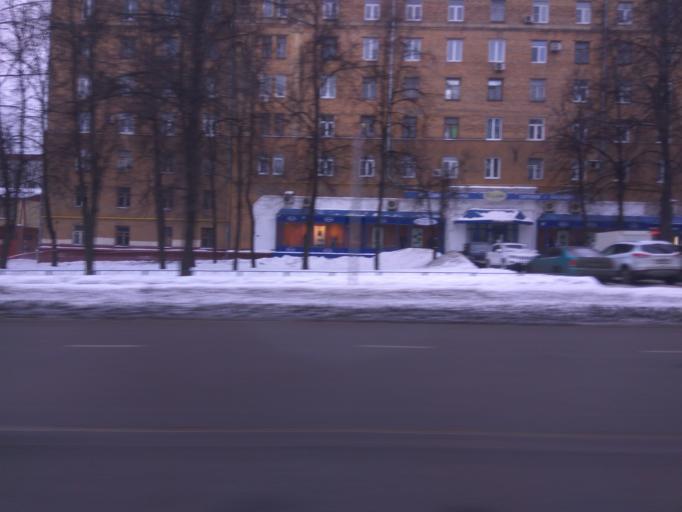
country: RU
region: Moskovskaya
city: Izmaylovo
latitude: 55.8010
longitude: 37.7990
